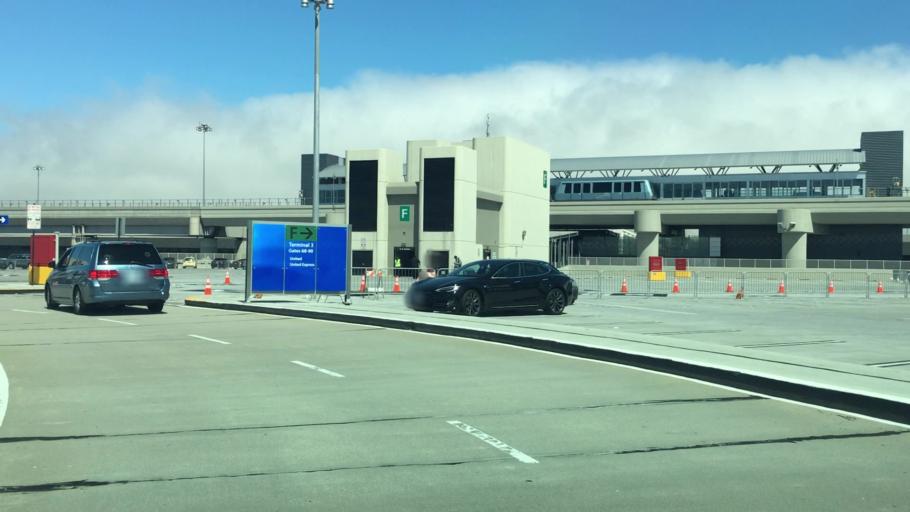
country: US
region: California
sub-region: San Mateo County
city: Millbrae
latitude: 37.6166
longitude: -122.3859
